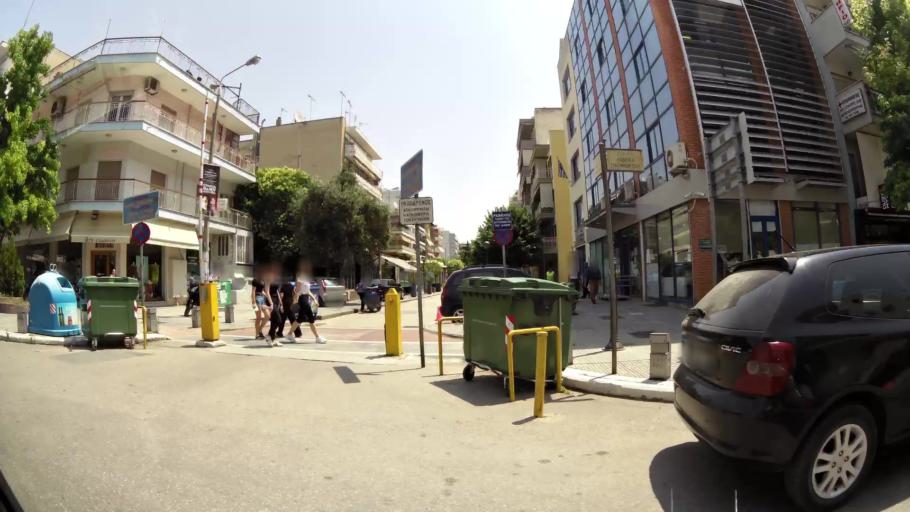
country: GR
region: Central Macedonia
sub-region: Nomos Thessalonikis
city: Menemeni
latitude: 40.6698
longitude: 22.8945
